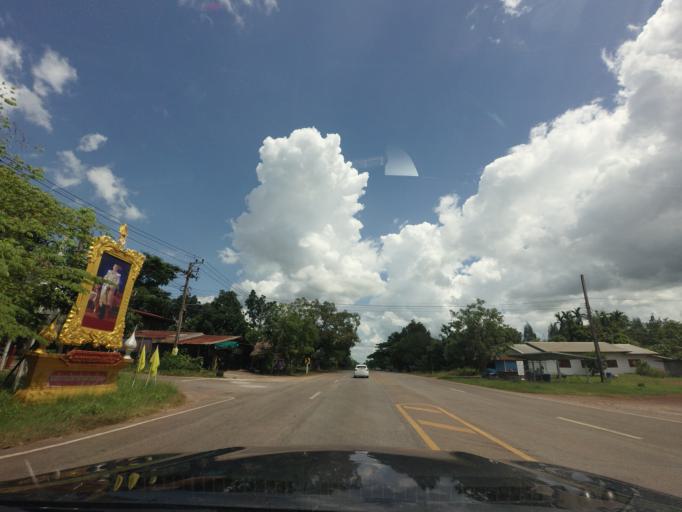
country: TH
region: Changwat Udon Thani
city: Ban Dung
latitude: 17.6861
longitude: 103.2024
